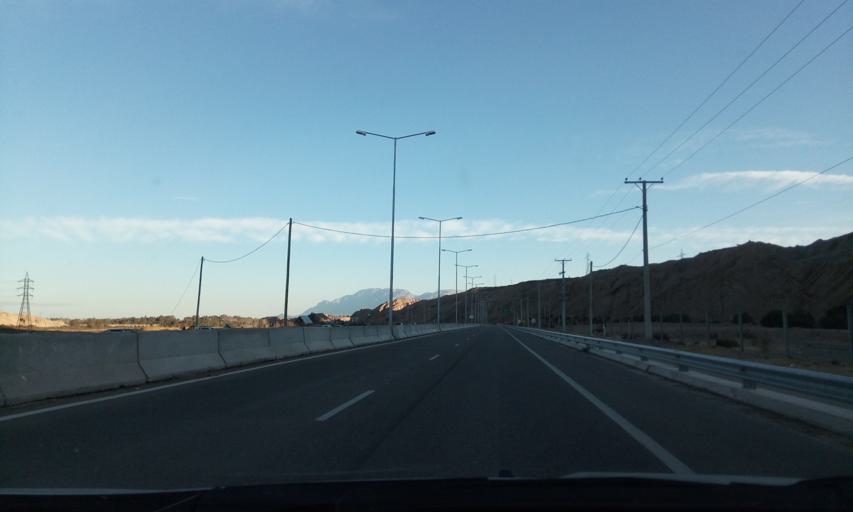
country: AR
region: San Juan
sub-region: Departamento de Rivadavia
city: Rivadavia
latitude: -31.4852
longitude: -68.6483
